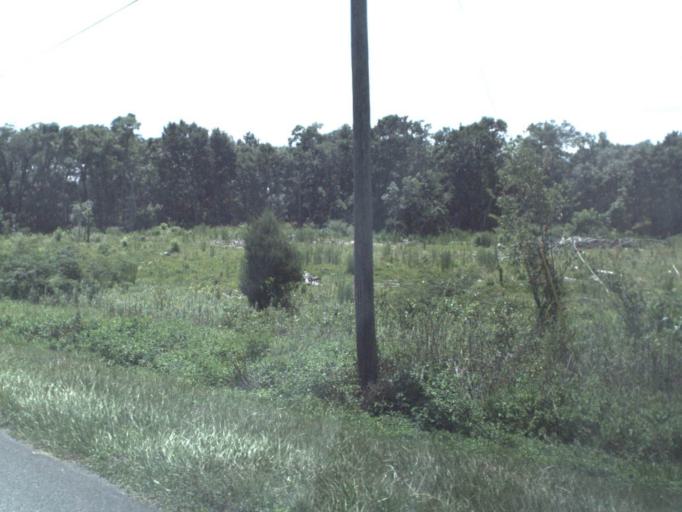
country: US
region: Florida
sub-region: Alachua County
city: Archer
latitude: 29.5408
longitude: -82.5130
